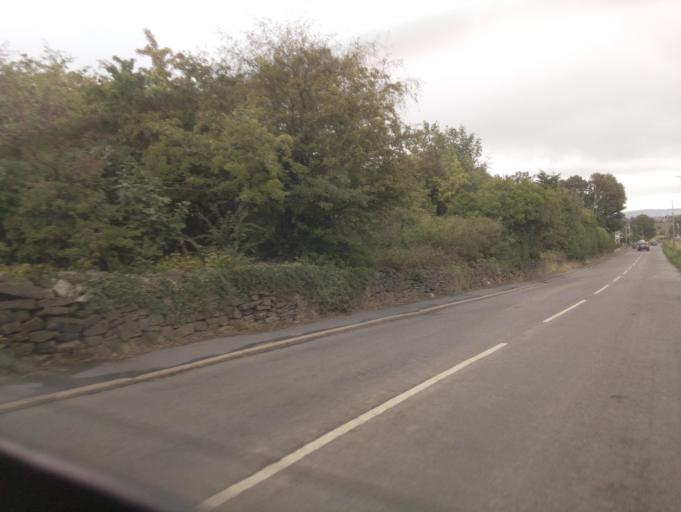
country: GB
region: England
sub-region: Kirklees
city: Shelley
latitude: 53.6144
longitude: -1.6508
